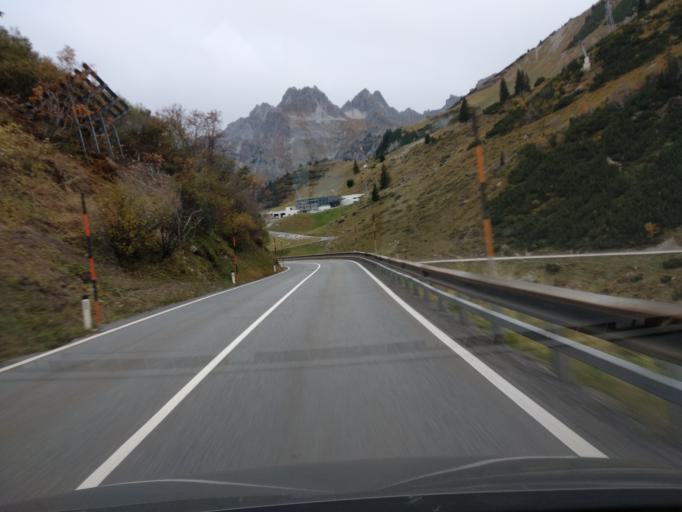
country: AT
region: Tyrol
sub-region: Politischer Bezirk Landeck
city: Sankt Anton am Arlberg
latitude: 47.1376
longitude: 10.1857
